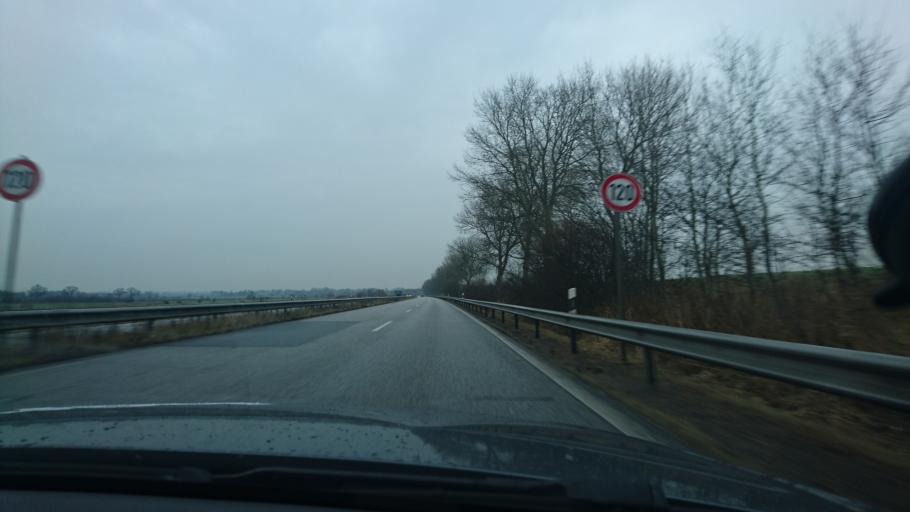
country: DE
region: Schleswig-Holstein
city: Altenkrempe
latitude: 54.1379
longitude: 10.8409
